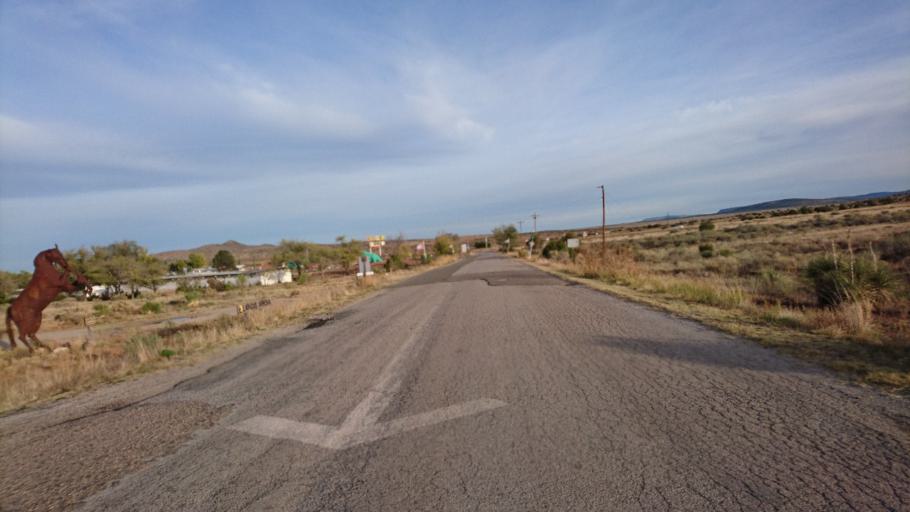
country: US
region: Arizona
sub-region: Mohave County
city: Peach Springs
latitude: 35.5273
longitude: -113.2293
